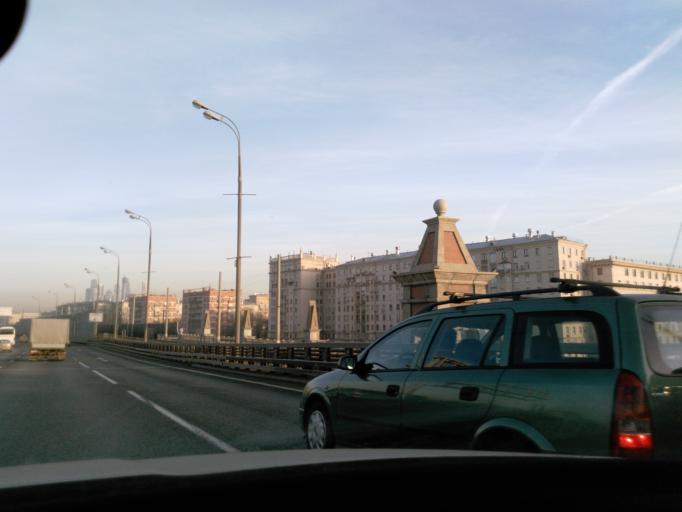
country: RU
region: Moscow
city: Novyye Cheremushki
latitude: 55.7144
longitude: 37.5768
